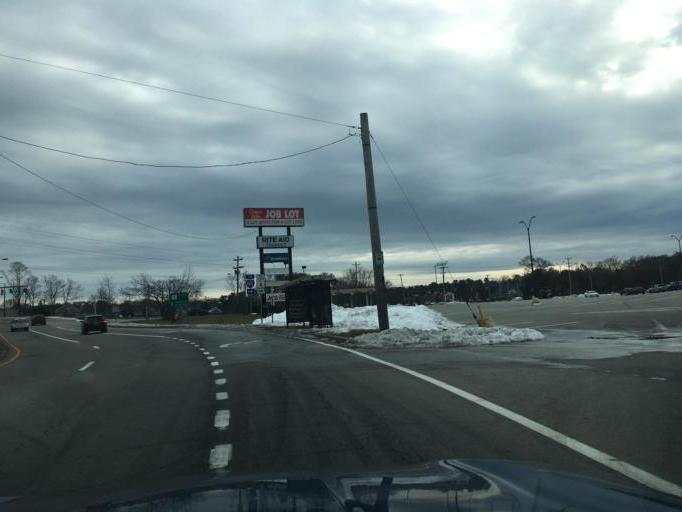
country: US
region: Rhode Island
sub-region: Kent County
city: East Greenwich
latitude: 41.6340
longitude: -71.4684
